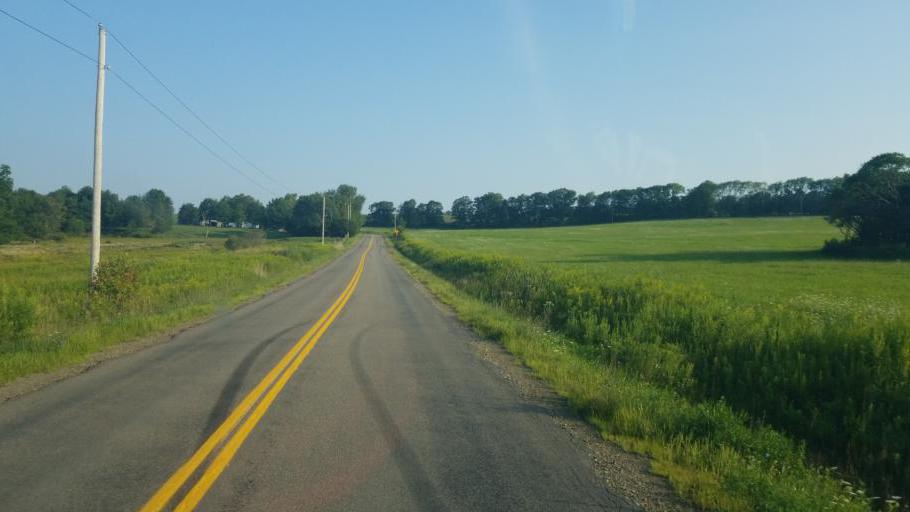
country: US
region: Pennsylvania
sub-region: Tioga County
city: Westfield
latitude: 42.0680
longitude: -77.6336
